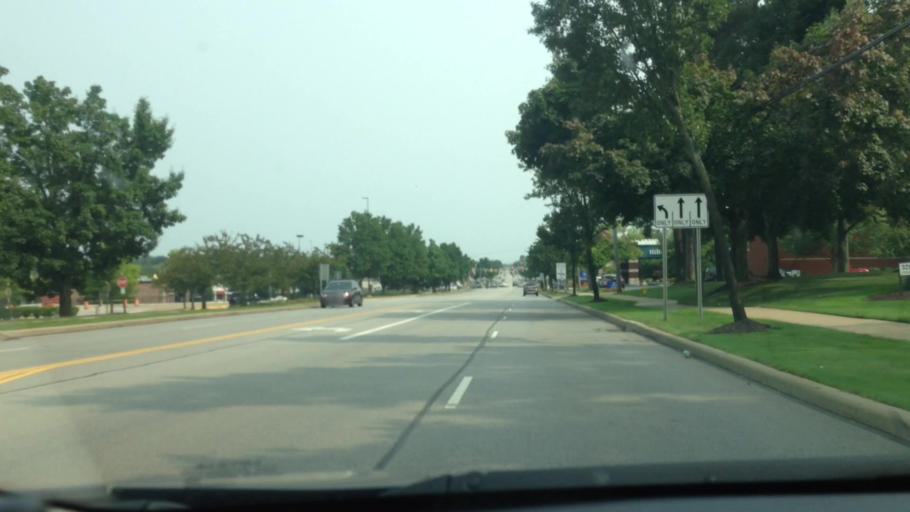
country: US
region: Ohio
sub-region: Summit County
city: Fairlawn
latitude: 41.1318
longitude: -81.6177
